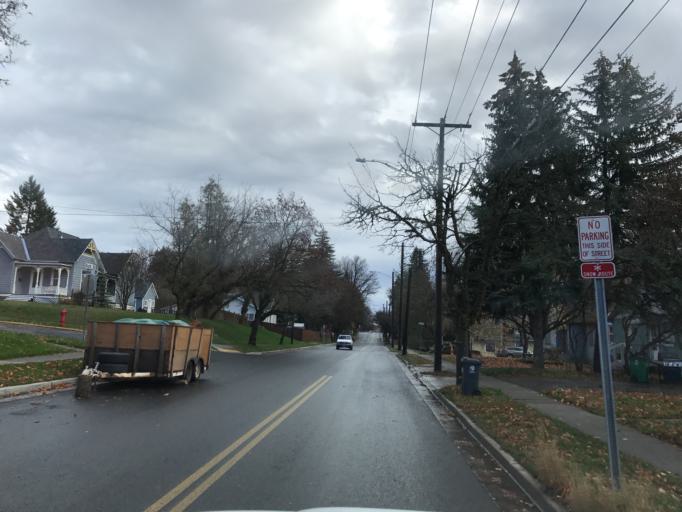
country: US
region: Idaho
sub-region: Latah County
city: Moscow
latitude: 46.7302
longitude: -116.9917
